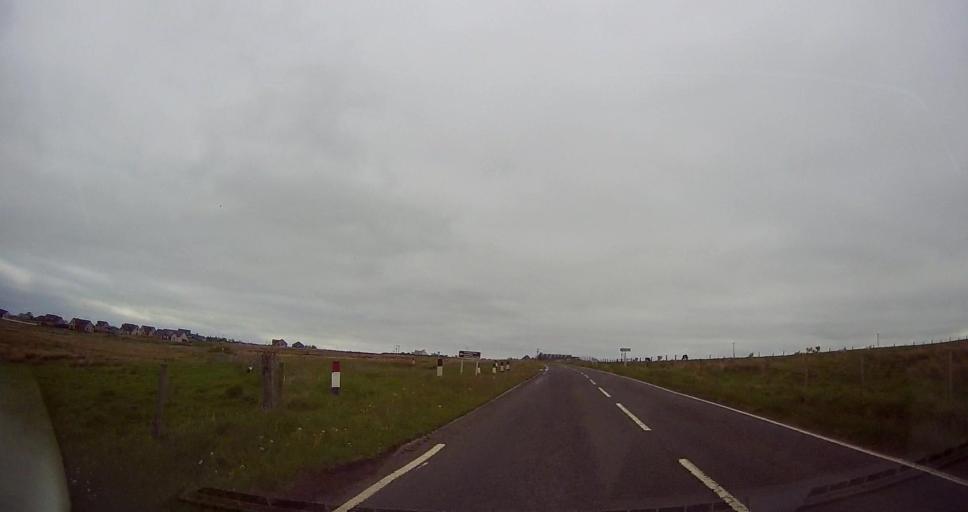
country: GB
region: Scotland
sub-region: Orkney Islands
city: Kirkwall
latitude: 58.9509
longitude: -2.8944
